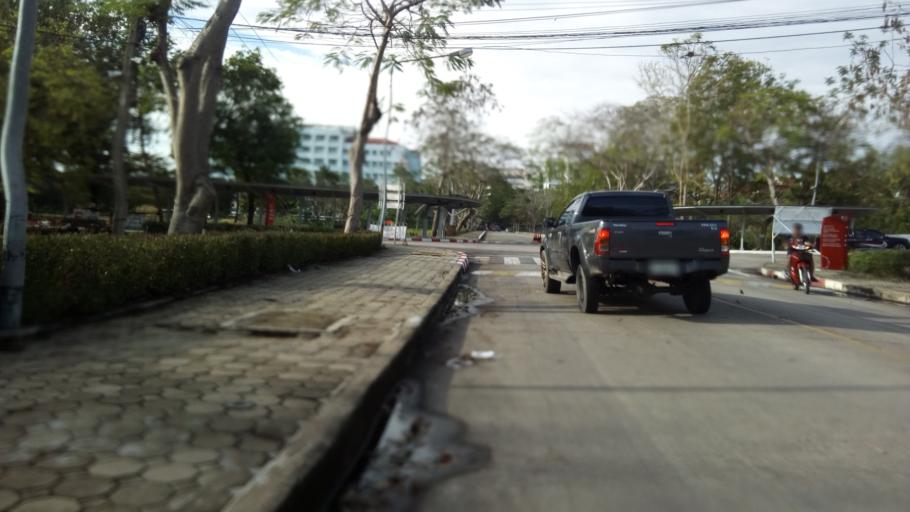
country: TH
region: Nakhon Nayok
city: Ongkharak
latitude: 14.1057
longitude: 100.9867
